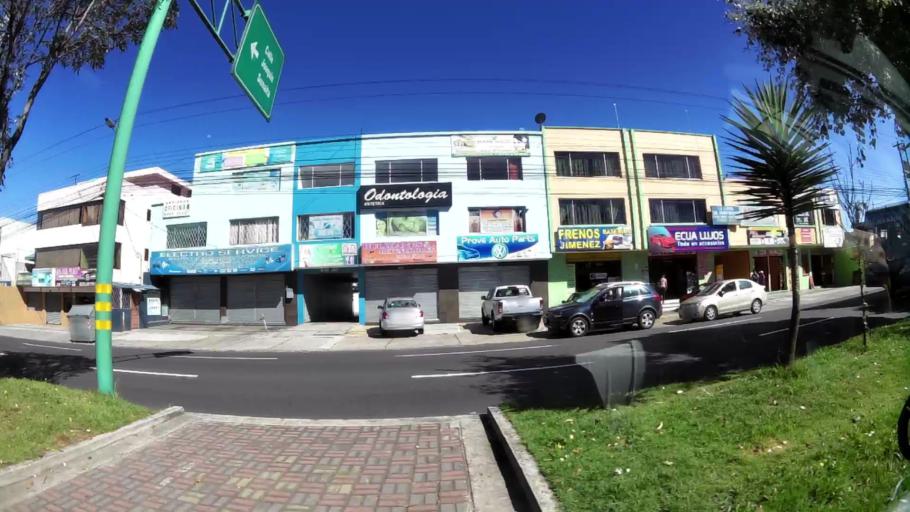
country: EC
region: Pichincha
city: Quito
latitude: -0.1509
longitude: -78.4762
